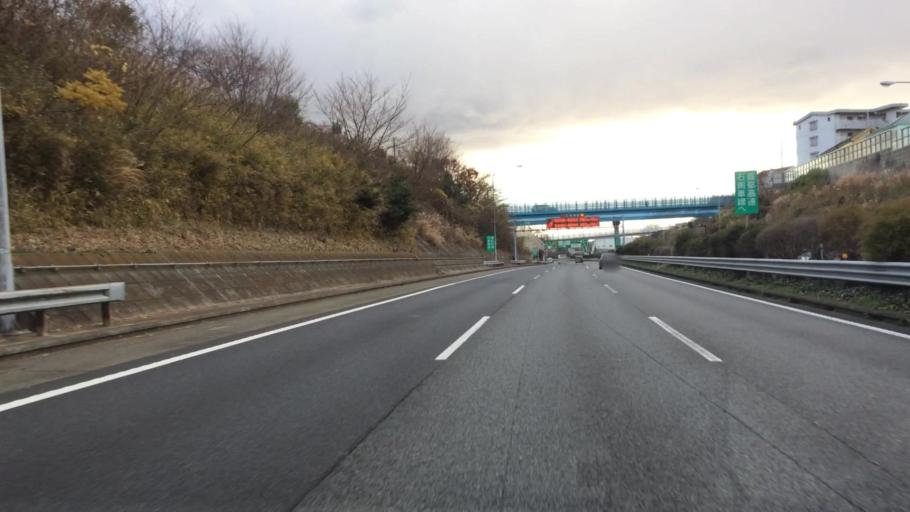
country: JP
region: Kanagawa
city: Yokohama
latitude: 35.4915
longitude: 139.5924
